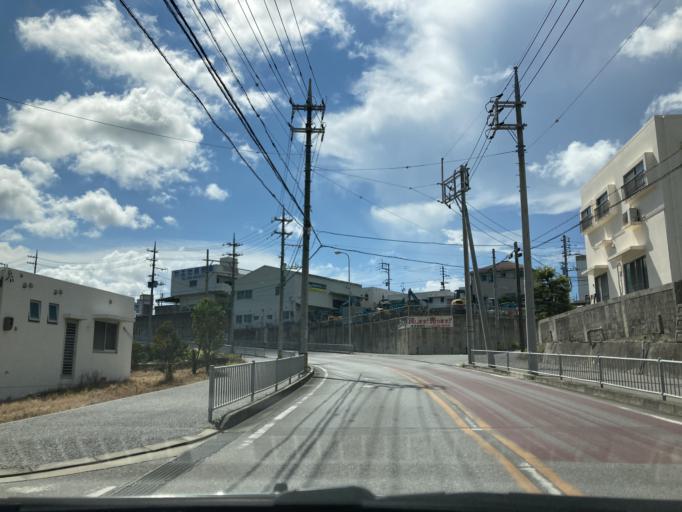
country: JP
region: Okinawa
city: Tomigusuku
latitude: 26.1649
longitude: 127.7227
